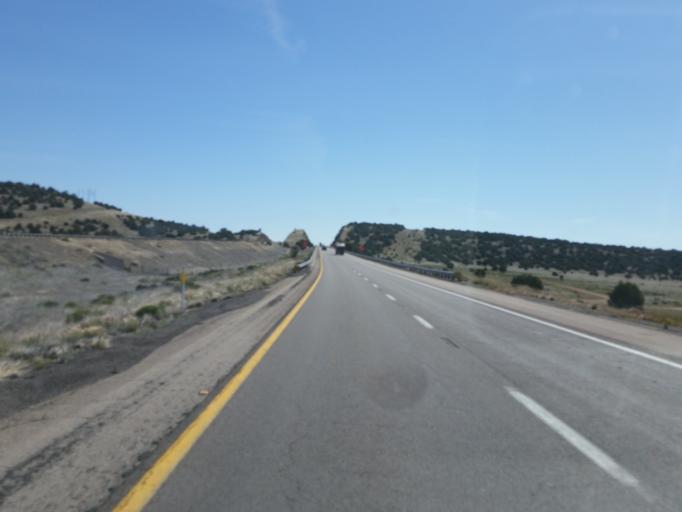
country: US
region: Arizona
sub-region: Mohave County
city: Peach Springs
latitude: 35.2351
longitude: -113.2098
